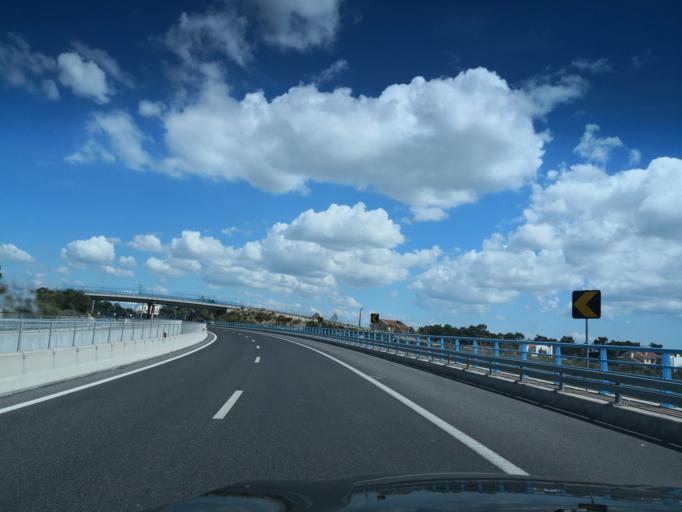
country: PT
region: Setubal
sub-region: Almada
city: Charneca
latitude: 38.6106
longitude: -9.1652
